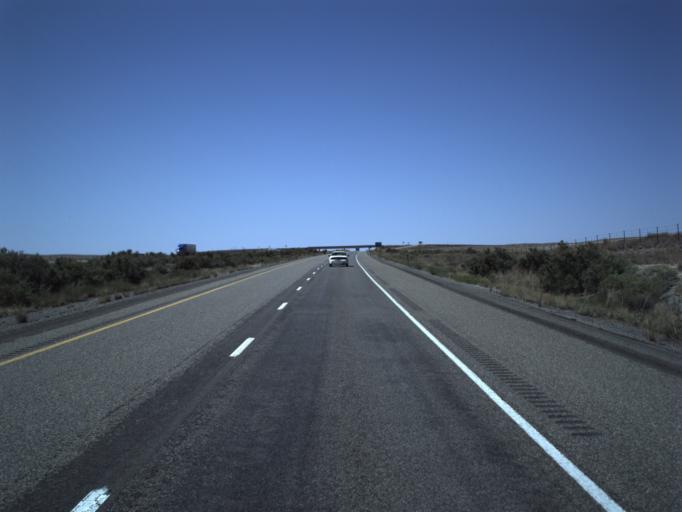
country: US
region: Colorado
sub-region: Mesa County
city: Loma
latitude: 39.1203
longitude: -109.1745
